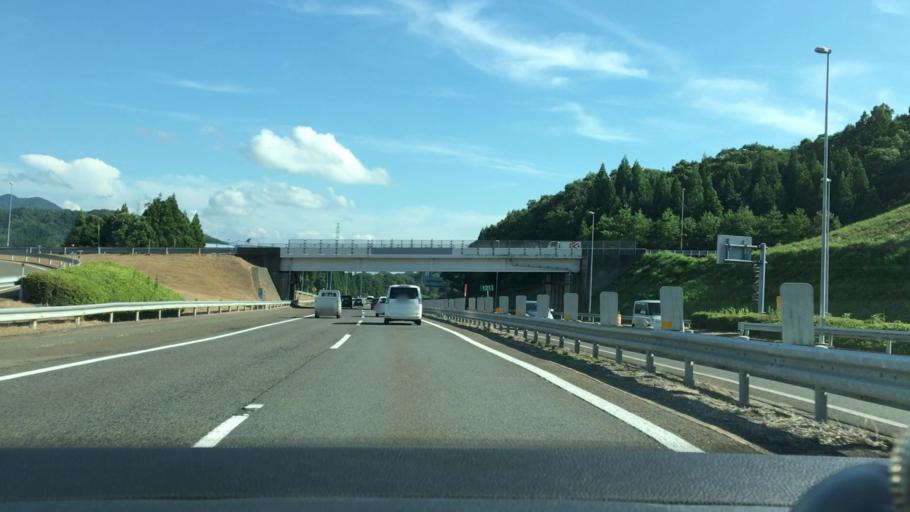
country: JP
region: Fukui
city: Maruoka
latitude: 36.2361
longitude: 136.2803
